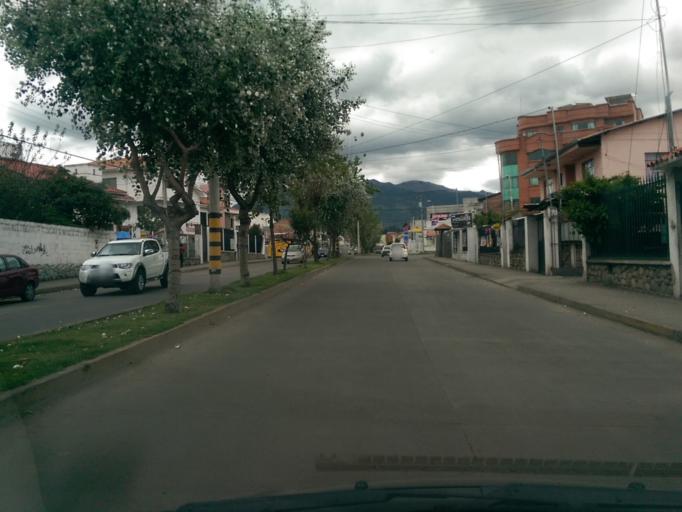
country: EC
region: Azuay
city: Cuenca
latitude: -2.9104
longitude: -79.0212
